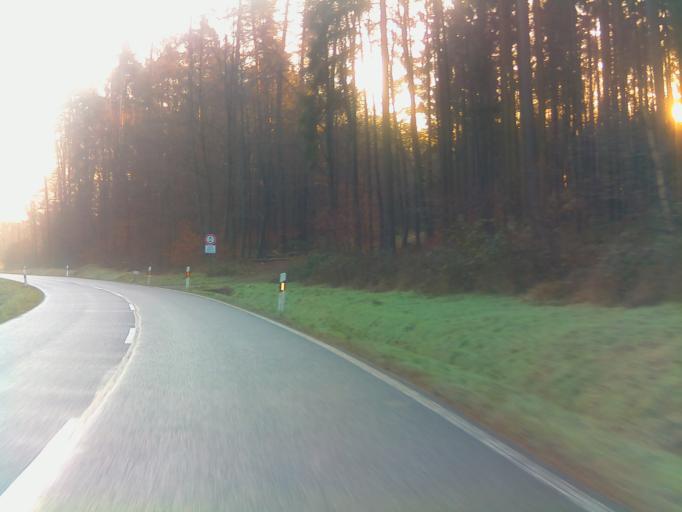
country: DE
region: Bavaria
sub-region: Regierungsbezirk Unterfranken
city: Eichenbuhl
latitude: 49.6784
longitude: 9.3062
